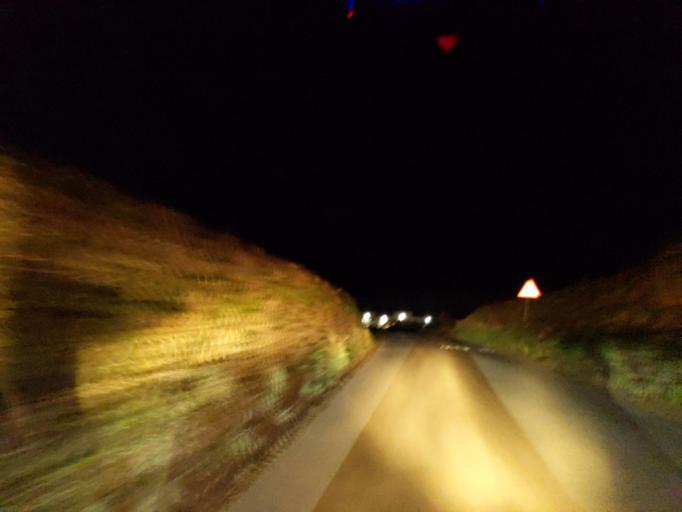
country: GB
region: England
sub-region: Cornwall
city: Torpoint
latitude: 50.3514
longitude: -4.2315
